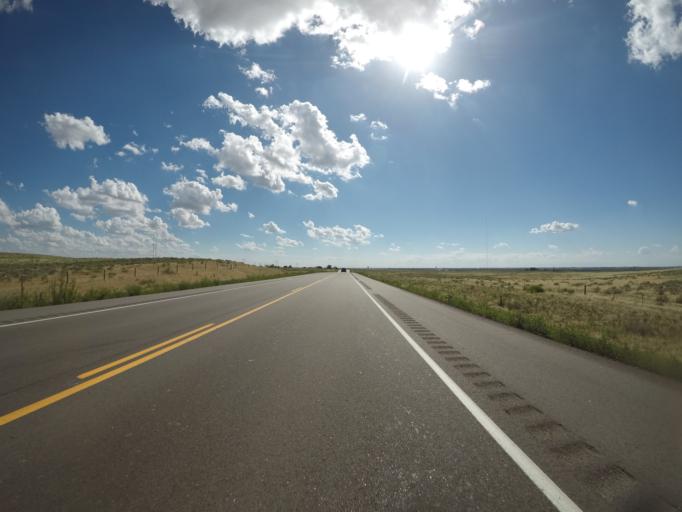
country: US
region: Colorado
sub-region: Logan County
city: Sterling
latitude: 40.6274
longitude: -103.1508
